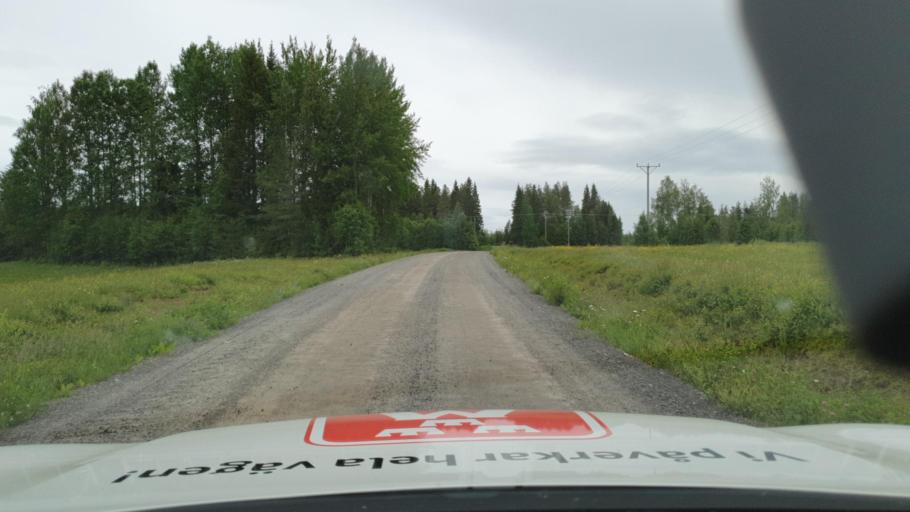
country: SE
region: Vaesterbotten
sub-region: Skelleftea Kommun
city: Burtraesk
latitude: 64.3612
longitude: 20.6159
